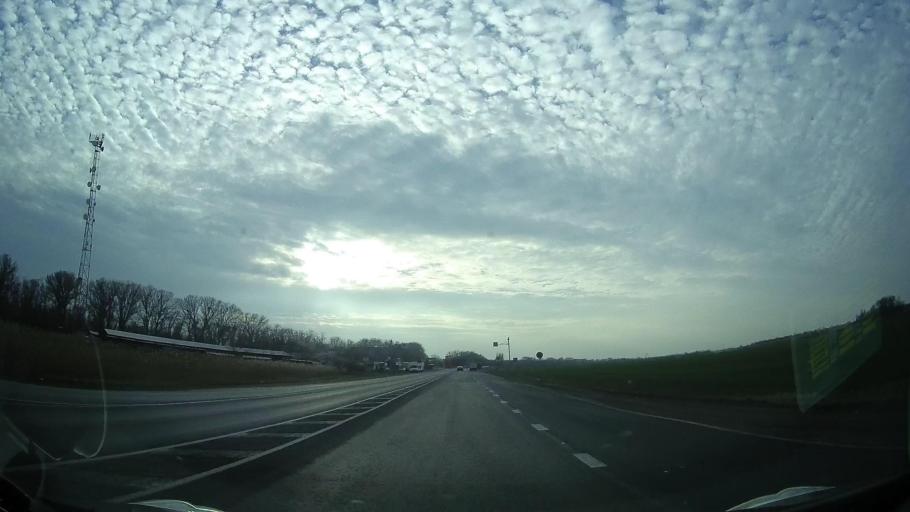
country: RU
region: Rostov
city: Bagayevskaya
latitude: 47.1665
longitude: 40.2706
